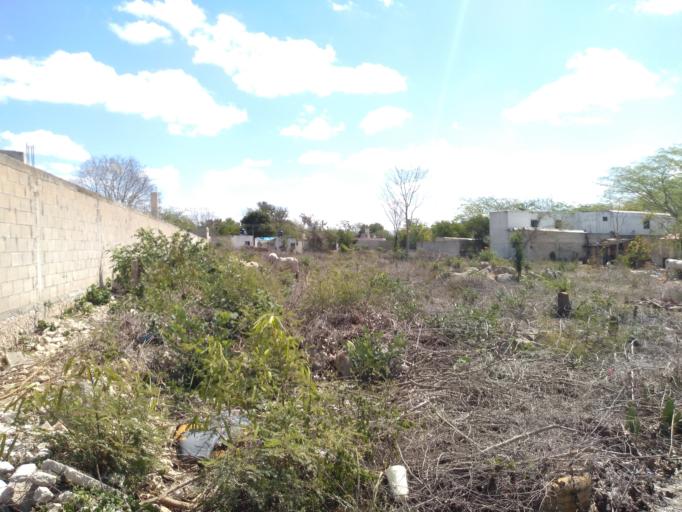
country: MX
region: Yucatan
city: Itzincab Palomeque
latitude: 20.9235
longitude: -89.6707
